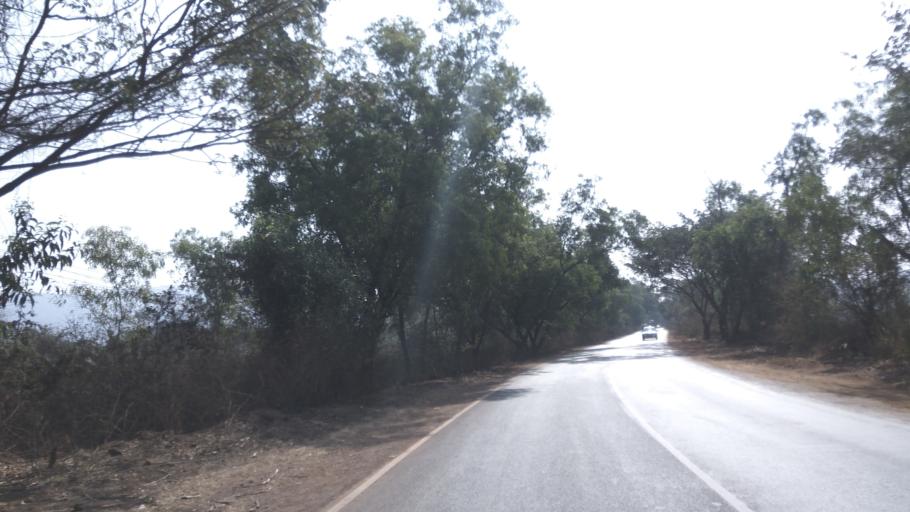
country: IN
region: Goa
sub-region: North Goa
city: Palle
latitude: 15.4146
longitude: 74.0786
